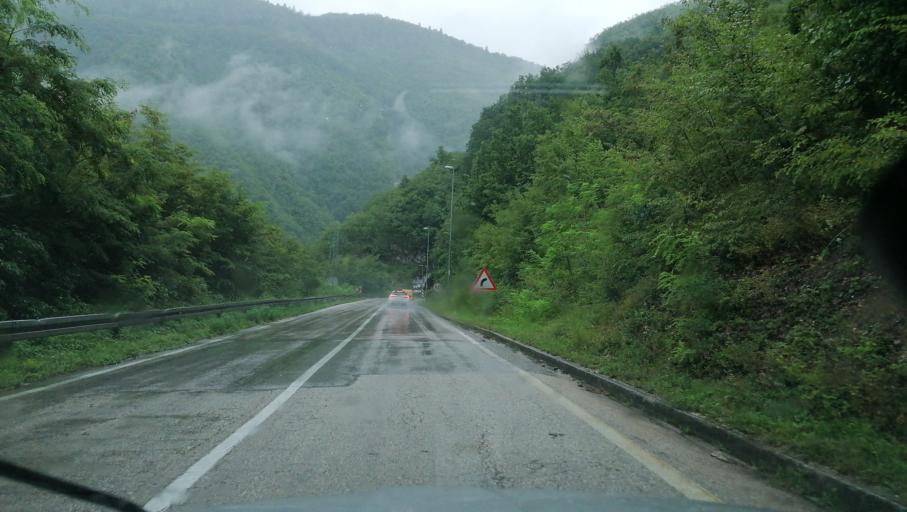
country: BA
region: Republika Srpska
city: Cajnice
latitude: 43.6825
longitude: 19.1495
